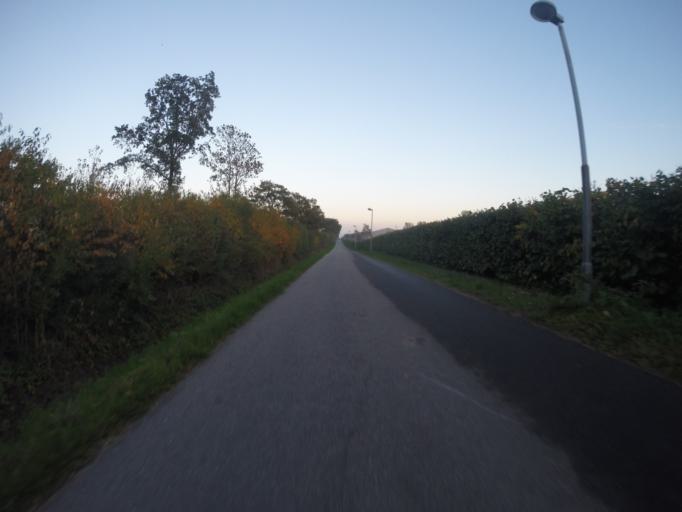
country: DK
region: Capital Region
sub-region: Hoje-Taastrup Kommune
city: Taastrup
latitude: 55.6674
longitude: 12.2988
